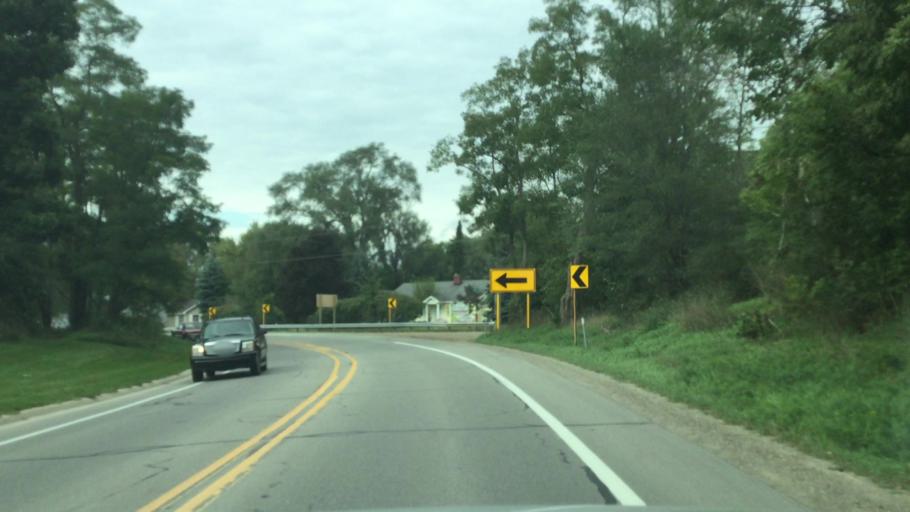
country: US
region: Michigan
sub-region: Livingston County
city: Brighton
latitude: 42.4631
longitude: -83.8277
